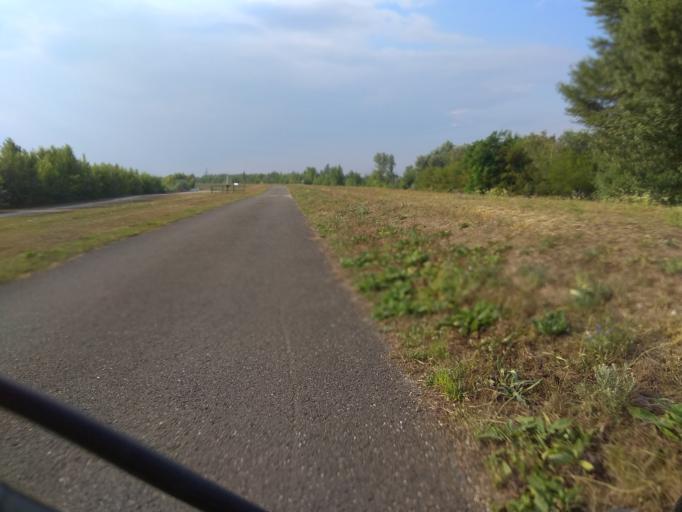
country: SK
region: Trnavsky
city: Gabcikovo
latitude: 47.8729
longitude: 17.5541
